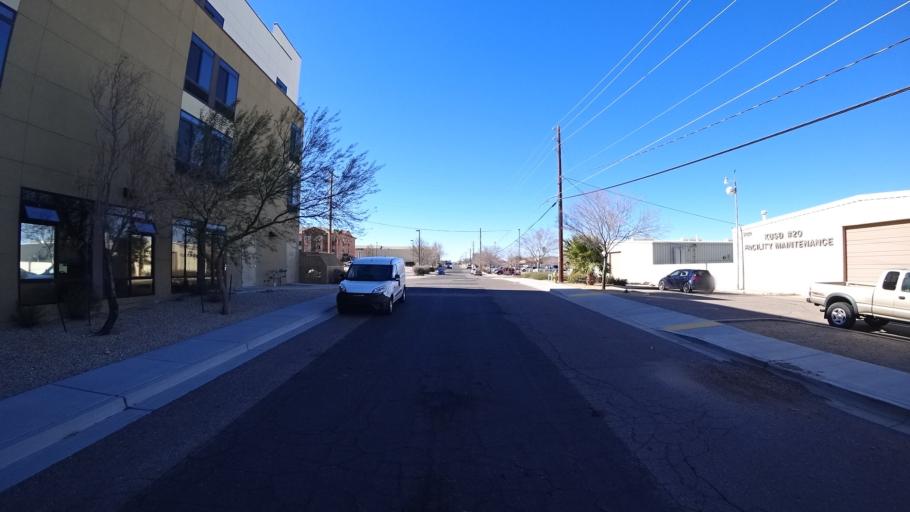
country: US
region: Arizona
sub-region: Mohave County
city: Kingman
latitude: 35.2154
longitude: -114.0142
